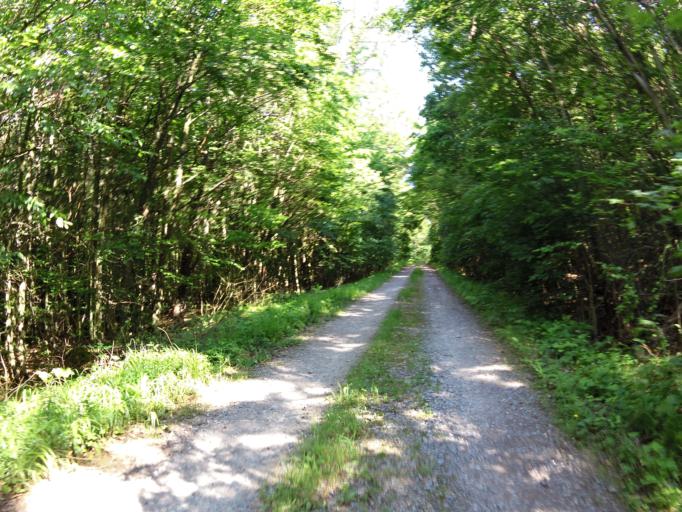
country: DE
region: Bavaria
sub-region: Regierungsbezirk Unterfranken
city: Reichenberg
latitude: 49.7344
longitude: 9.8975
